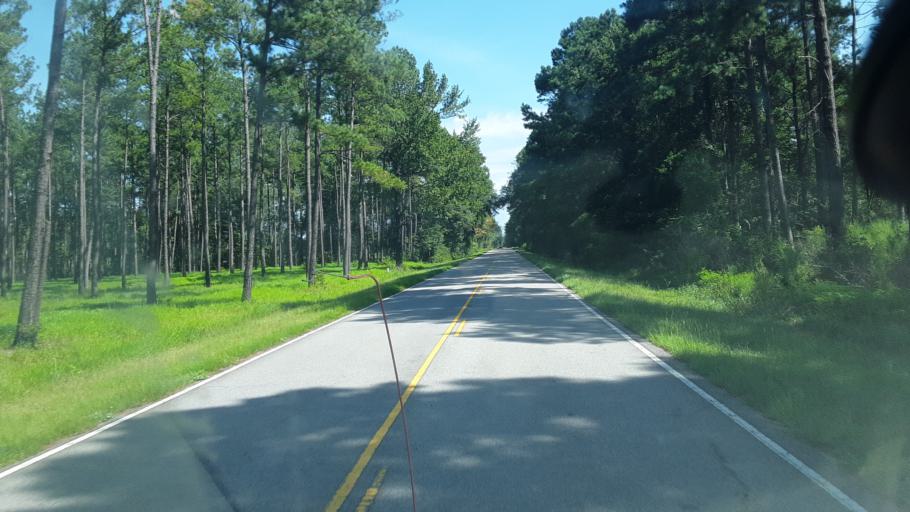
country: US
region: South Carolina
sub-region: Hampton County
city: Hampton
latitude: 32.9979
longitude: -81.0498
